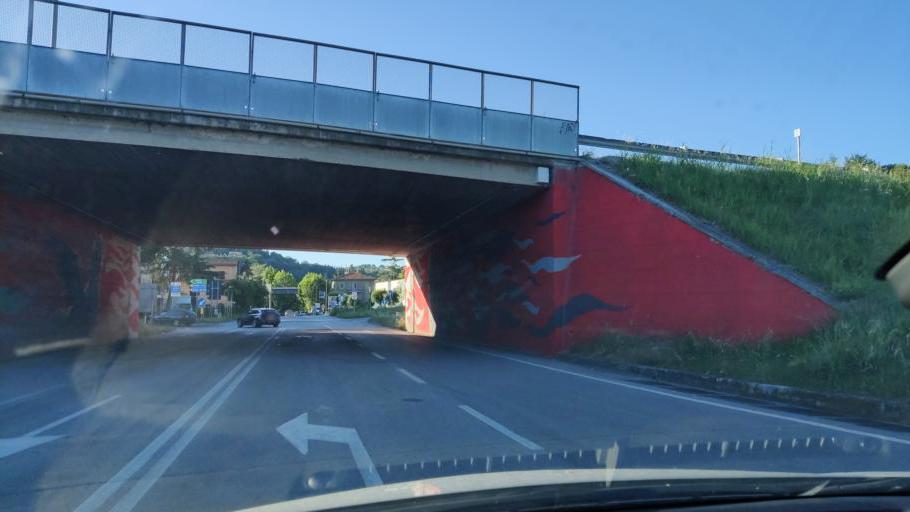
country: IT
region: Umbria
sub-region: Provincia di Perugia
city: Via Lippia
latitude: 43.0871
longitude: 12.4466
